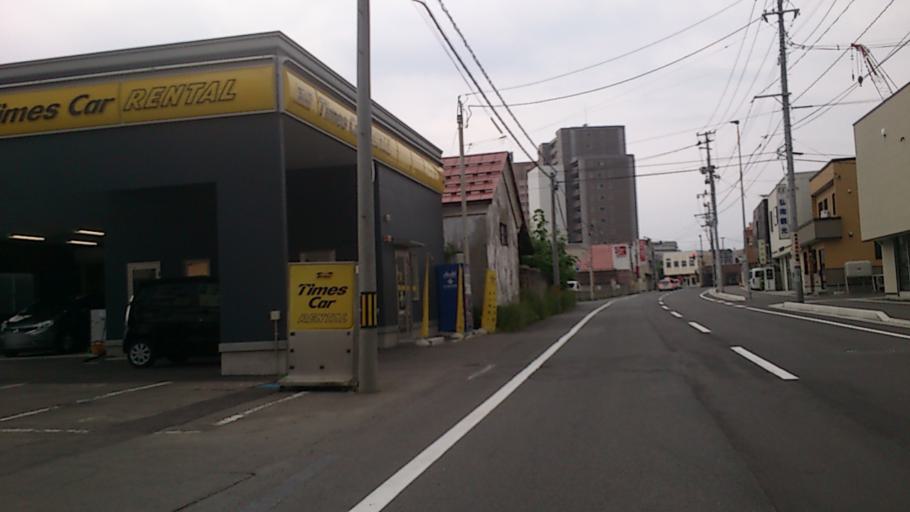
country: JP
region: Aomori
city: Hirosaki
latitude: 40.6016
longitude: 140.4827
